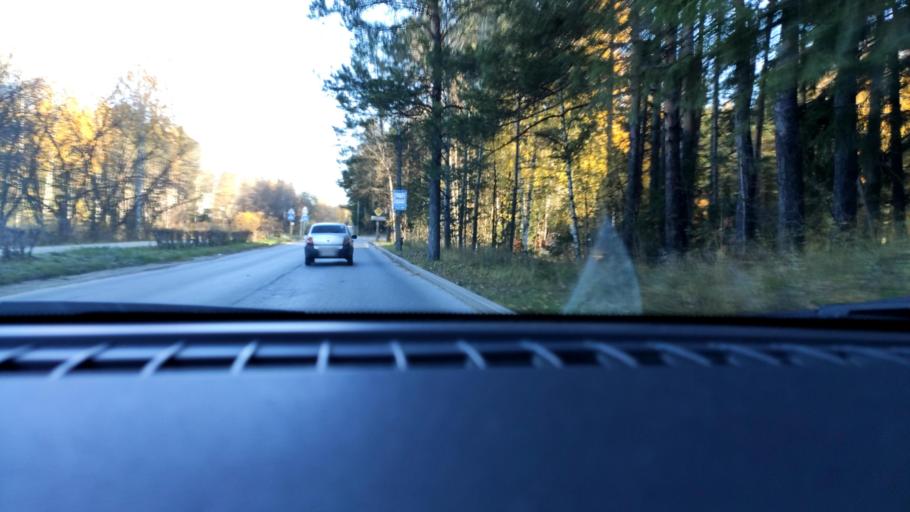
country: RU
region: Perm
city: Perm
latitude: 58.0509
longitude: 56.2138
